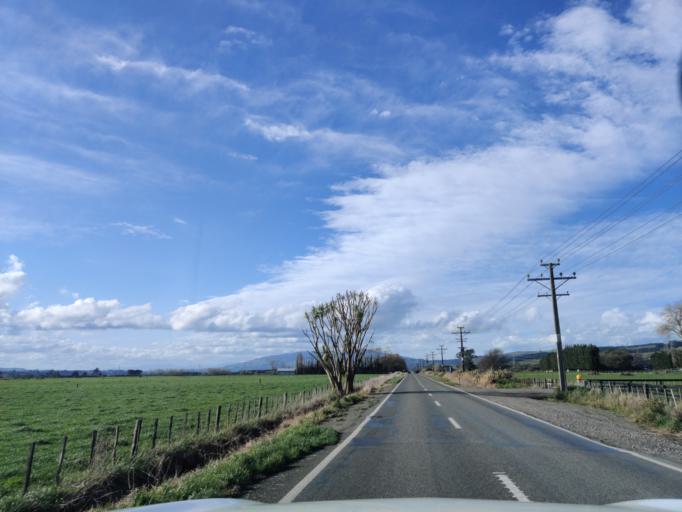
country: NZ
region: Manawatu-Wanganui
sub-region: Palmerston North City
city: Palmerston North
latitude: -40.3511
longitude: 175.6971
